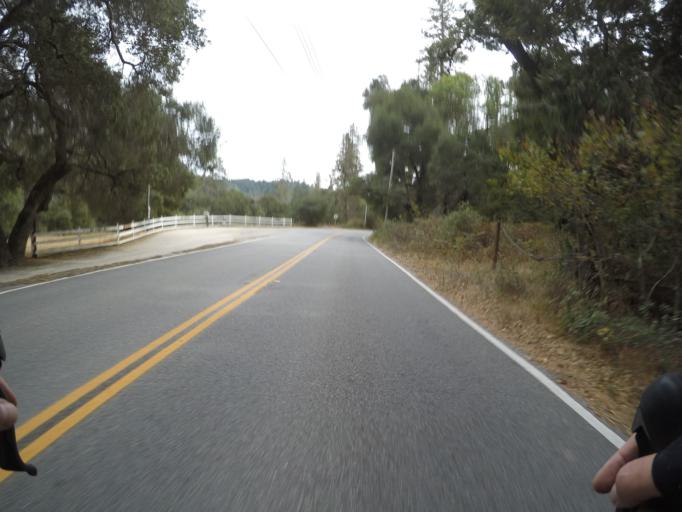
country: US
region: California
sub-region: Santa Cruz County
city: Ben Lomond
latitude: 37.0817
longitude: -122.0635
